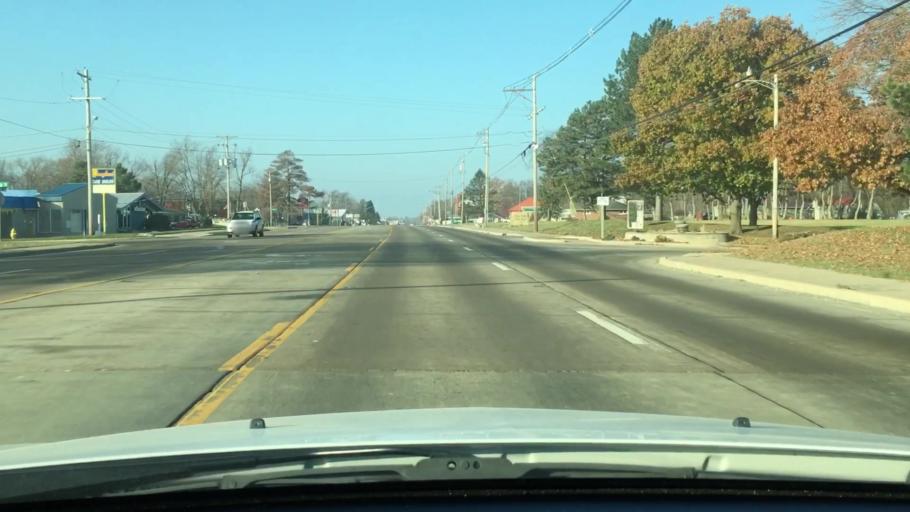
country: US
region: Illinois
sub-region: Woodford County
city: Germantown Hills
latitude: 40.6927
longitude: -89.4857
